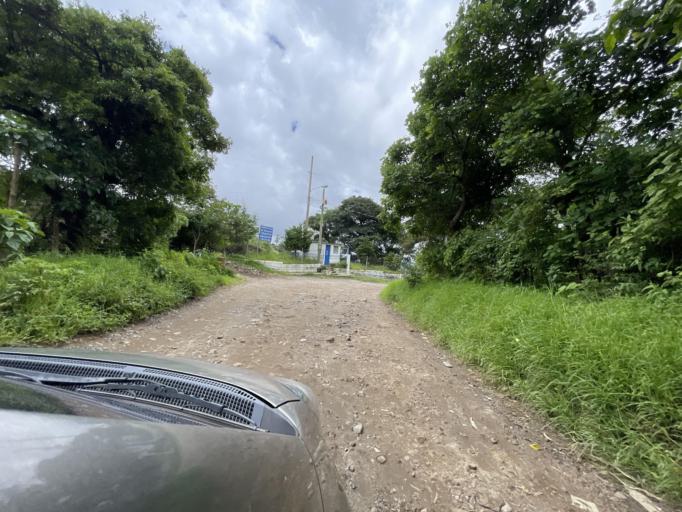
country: GT
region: Guatemala
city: Mixco
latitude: 14.6403
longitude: -90.6249
